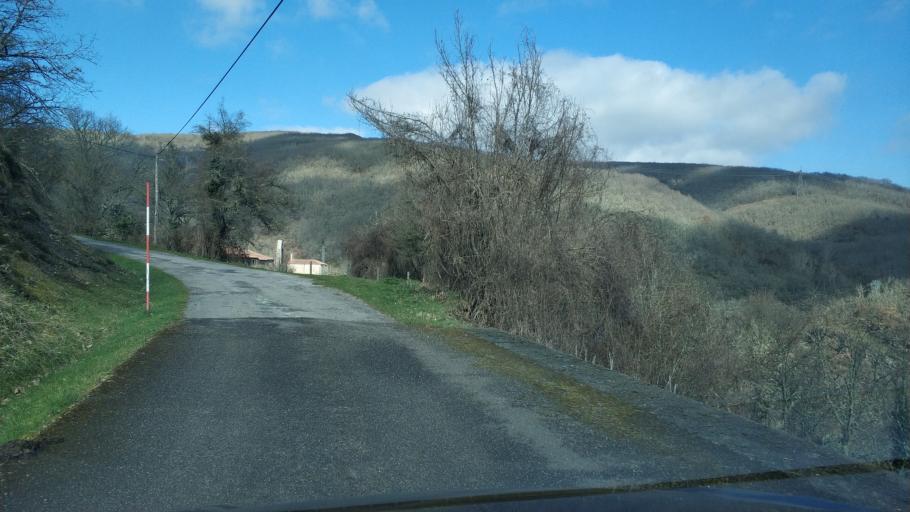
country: ES
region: Castille and Leon
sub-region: Provincia de Burgos
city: Arija
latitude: 42.9056
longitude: -4.0277
